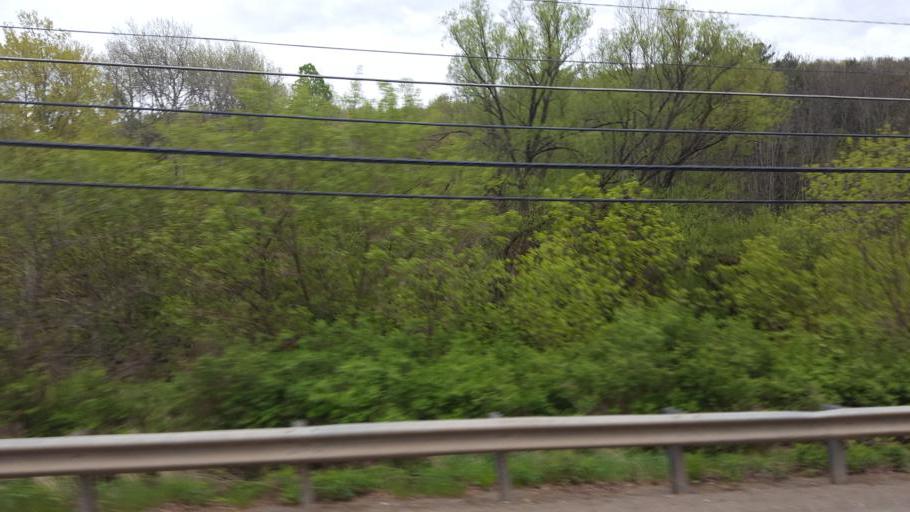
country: US
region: Pennsylvania
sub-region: Tioga County
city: Westfield
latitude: 41.9180
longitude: -77.5482
